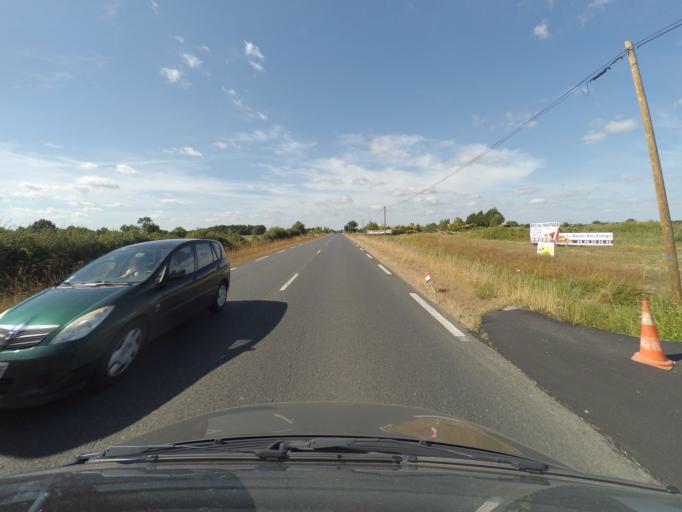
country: FR
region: Pays de la Loire
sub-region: Departement de la Loire-Atlantique
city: Les Sorinieres
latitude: 47.1046
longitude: -1.5361
